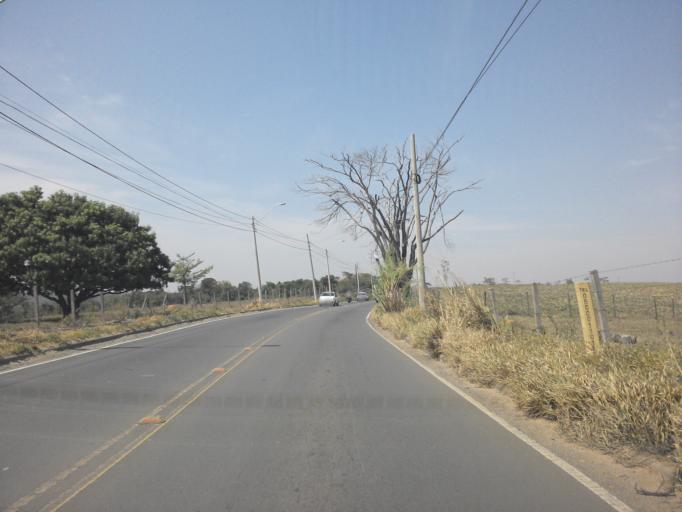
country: BR
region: Sao Paulo
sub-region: Hortolandia
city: Hortolandia
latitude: -22.9145
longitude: -47.1949
